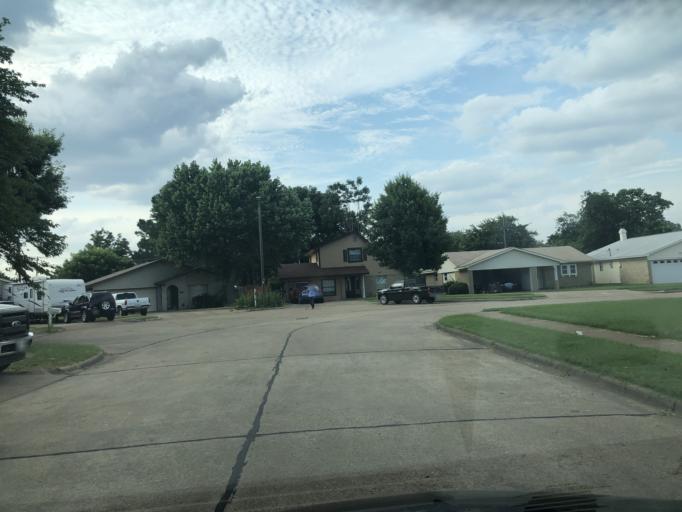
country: US
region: Texas
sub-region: Dallas County
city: Irving
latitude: 32.7913
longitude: -96.9766
